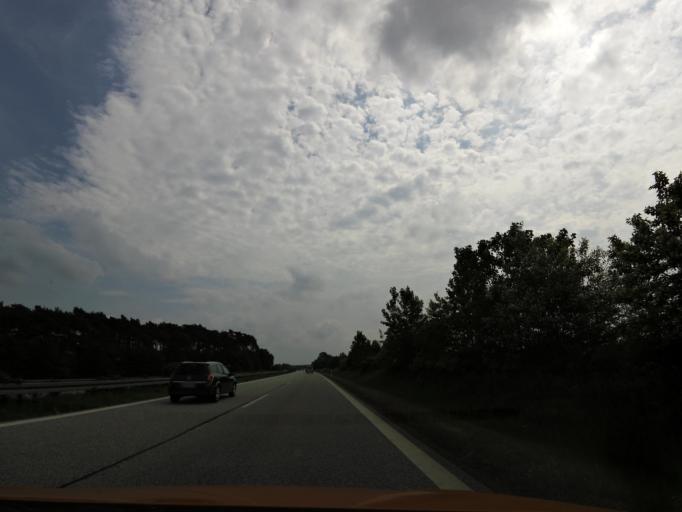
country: DE
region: Mecklenburg-Vorpommern
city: Mirow
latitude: 53.4568
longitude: 11.4969
